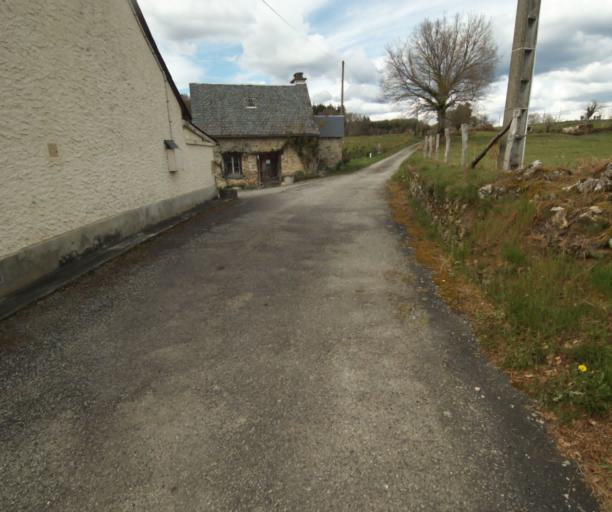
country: FR
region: Limousin
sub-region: Departement de la Correze
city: Argentat
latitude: 45.1854
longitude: 1.9345
